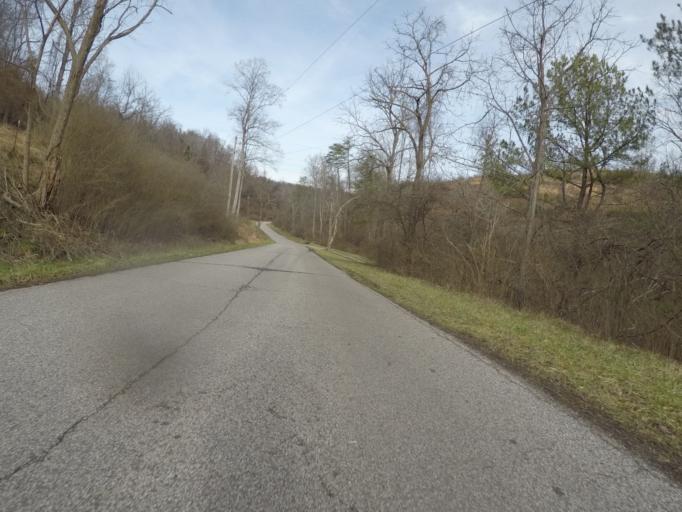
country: US
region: West Virginia
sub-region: Wayne County
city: Lavalette
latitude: 38.3480
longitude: -82.3727
